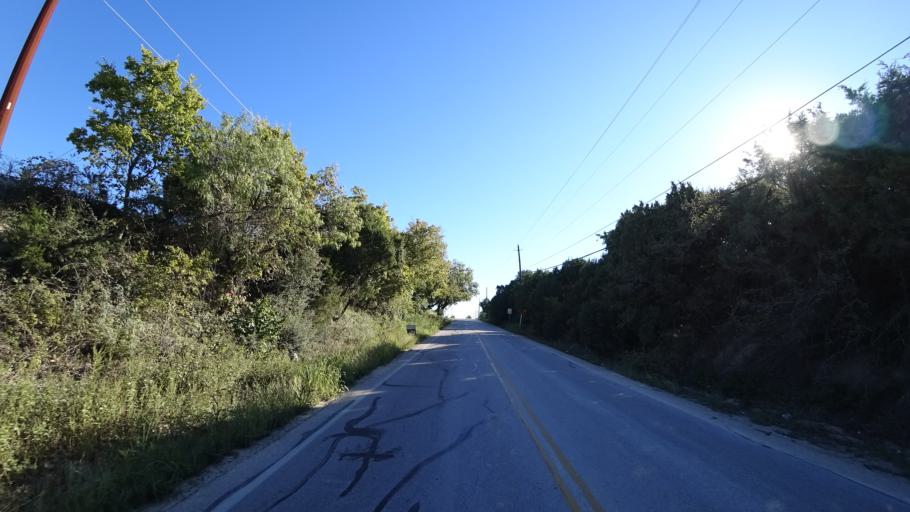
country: US
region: Texas
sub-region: Travis County
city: Manor
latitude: 30.3255
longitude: -97.6403
